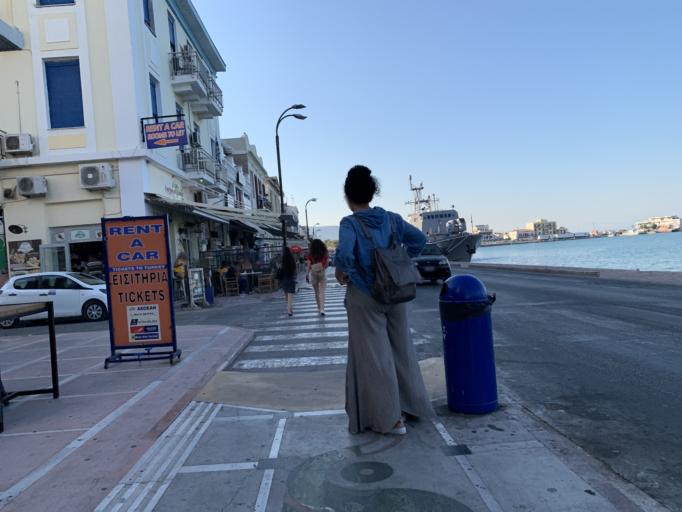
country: GR
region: North Aegean
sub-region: Chios
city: Chios
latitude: 38.3689
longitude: 26.1382
